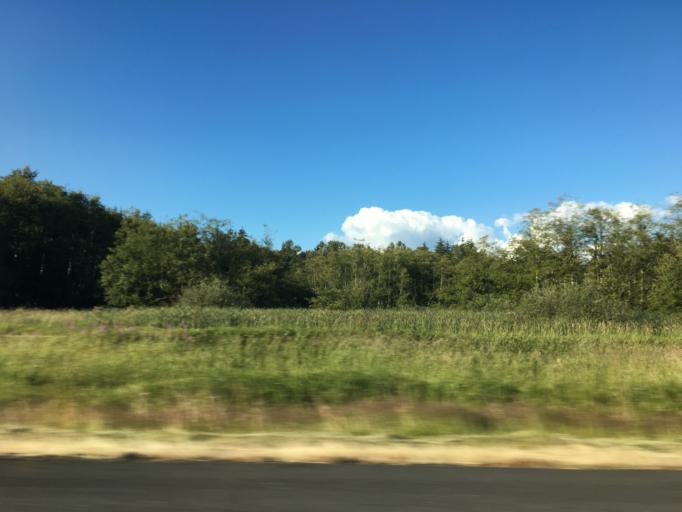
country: US
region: Washington
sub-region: Whatcom County
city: Birch Bay
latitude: 48.9546
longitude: -122.6915
